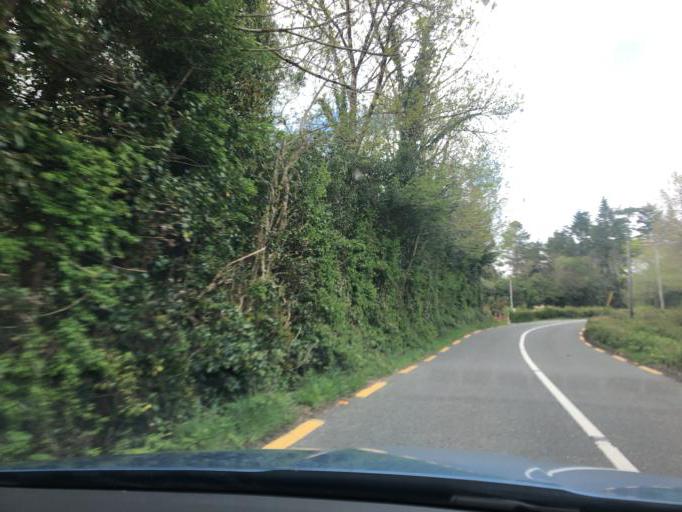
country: IE
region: Munster
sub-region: Ciarrai
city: Killorglin
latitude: 51.8205
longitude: -9.8766
